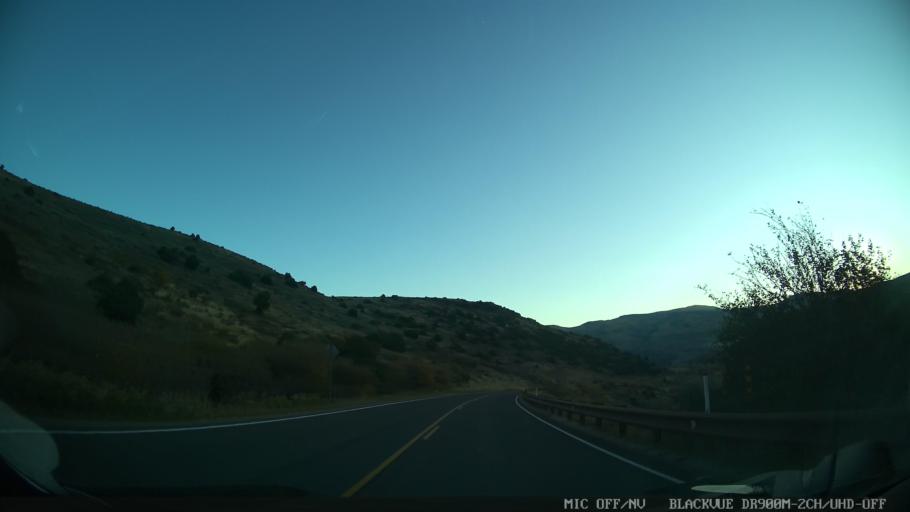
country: US
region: Colorado
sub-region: Eagle County
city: Edwards
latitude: 39.8156
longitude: -106.6632
